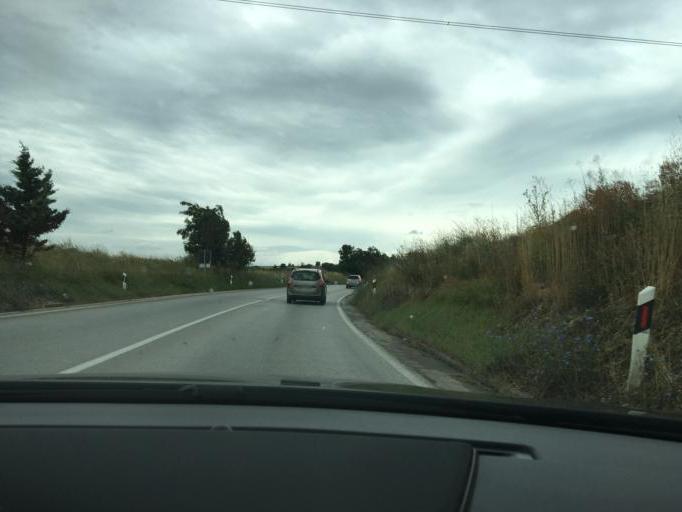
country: MK
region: Staro Nagoricane
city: Staro Nagorichane
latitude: 42.1732
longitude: 21.7827
